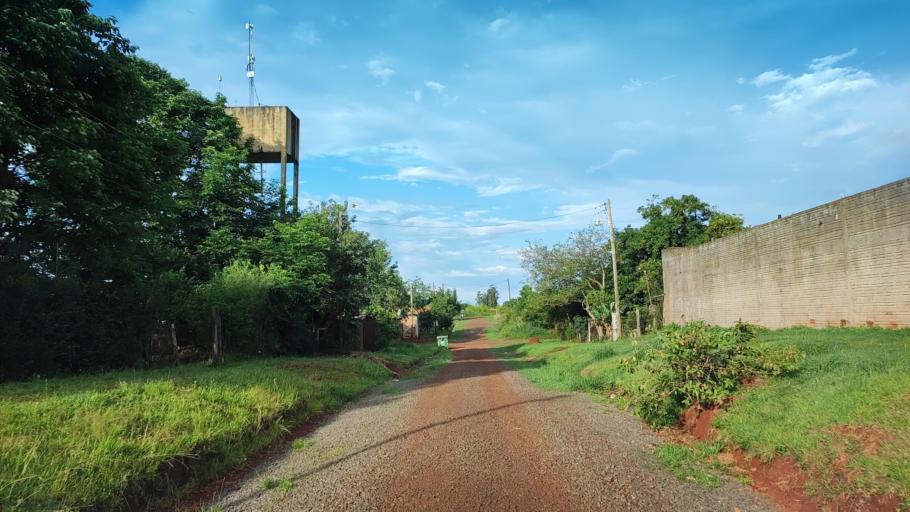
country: AR
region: Misiones
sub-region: Departamento de Capital
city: Posadas
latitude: -27.4461
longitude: -55.9617
